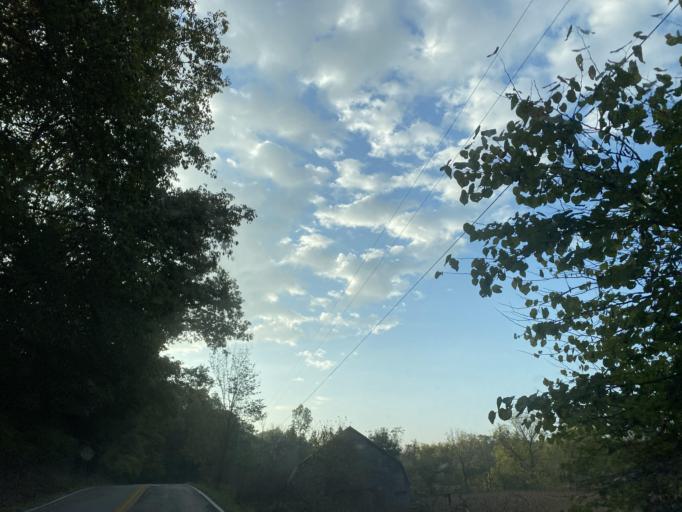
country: US
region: Kentucky
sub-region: Pendleton County
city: Falmouth
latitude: 38.7868
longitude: -84.3358
